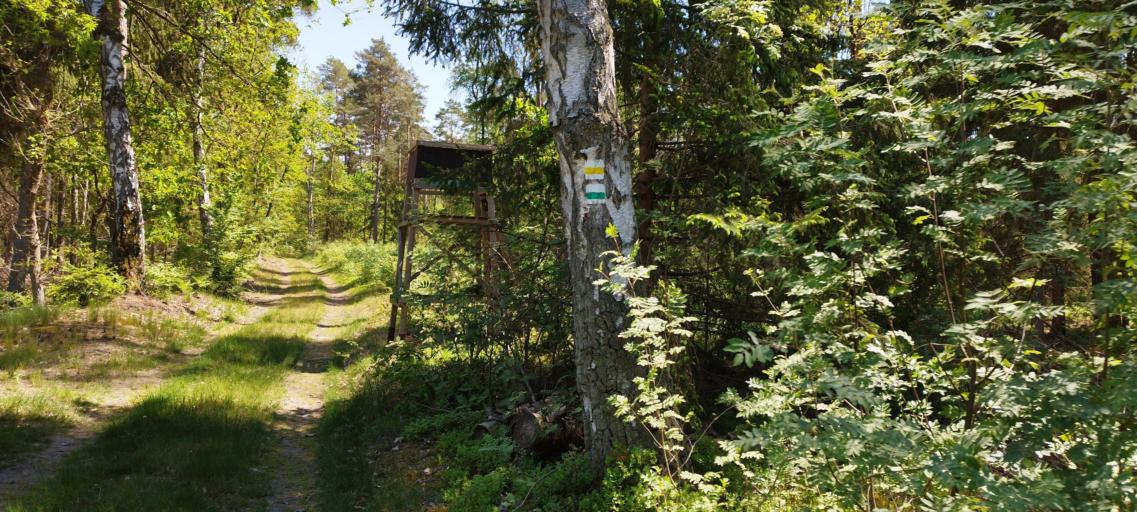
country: DE
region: Brandenburg
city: Rauen
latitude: 52.3830
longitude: 14.0087
